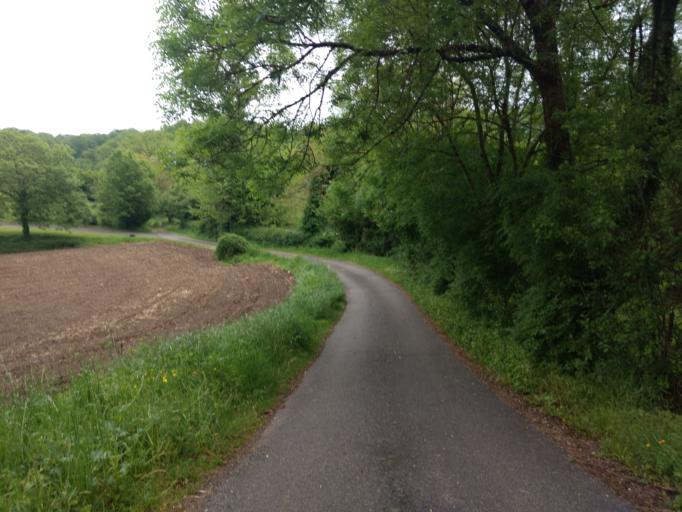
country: FR
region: Midi-Pyrenees
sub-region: Departement de l'Aveyron
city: Viviez
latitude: 44.5457
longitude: 2.1477
